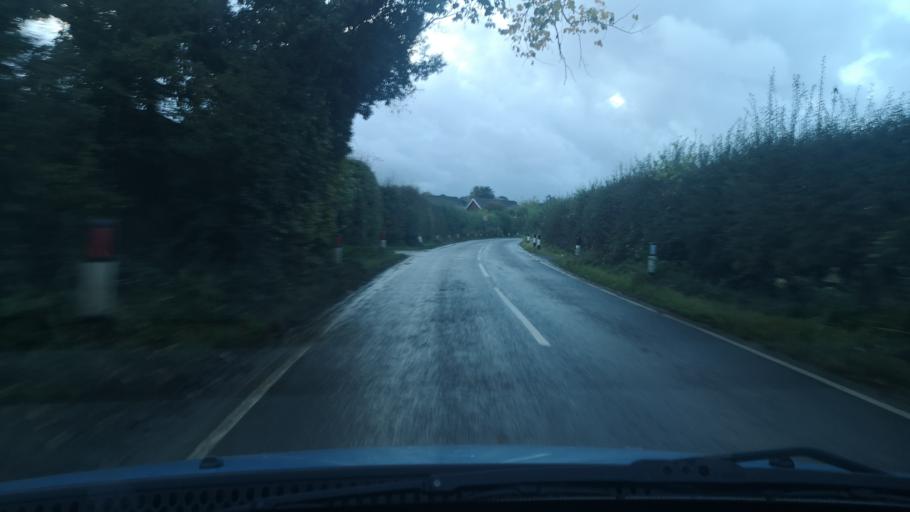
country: GB
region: England
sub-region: City and Borough of Wakefield
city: Low Ackworth
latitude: 53.6510
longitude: -1.3143
